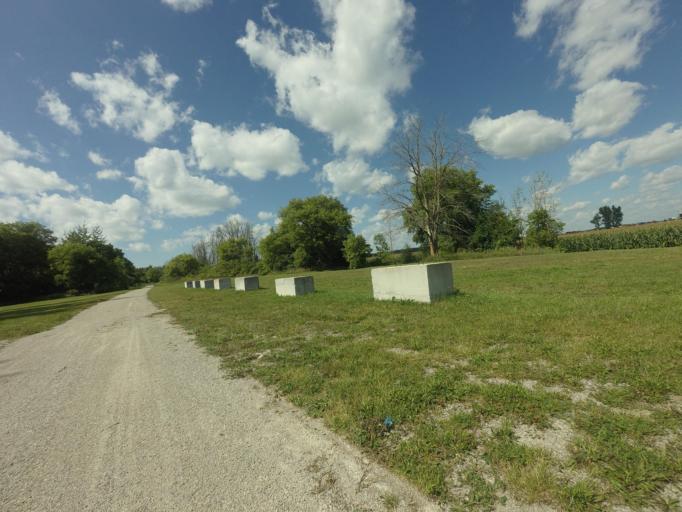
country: CA
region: Ontario
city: Huron East
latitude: 43.6806
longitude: -81.3006
